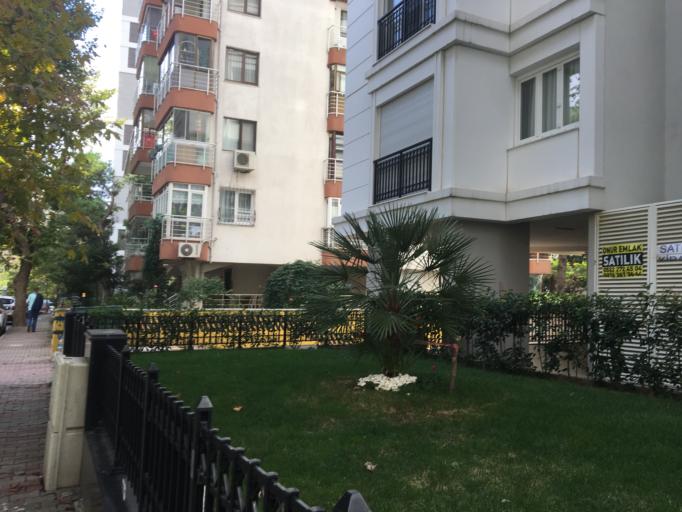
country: TR
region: Istanbul
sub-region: Atasehir
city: Atasehir
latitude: 40.9643
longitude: 29.0947
